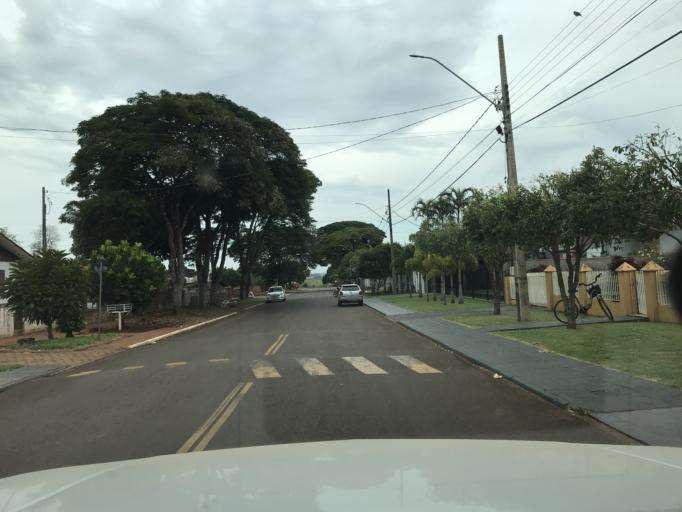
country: BR
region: Parana
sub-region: Marechal Candido Rondon
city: Marechal Candido Rondon
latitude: -24.4674
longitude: -53.9578
